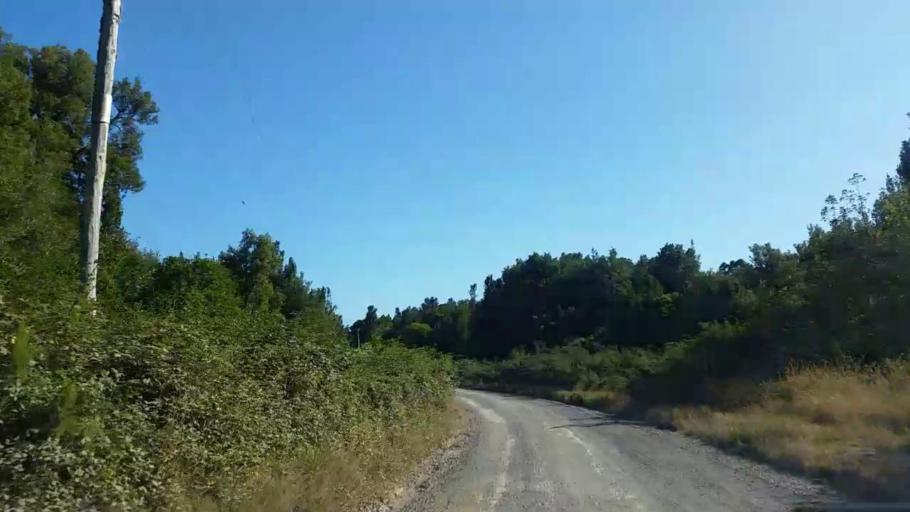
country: NZ
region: Bay of Plenty
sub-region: Kawerau District
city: Kawerau
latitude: -38.0150
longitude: 176.4896
